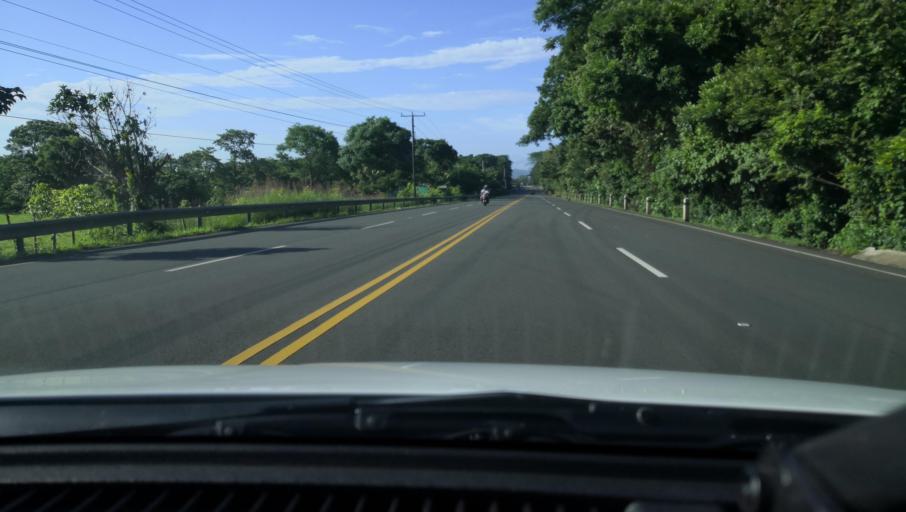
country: NI
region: Granada
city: Nandaime
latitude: 11.7833
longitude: -86.0557
